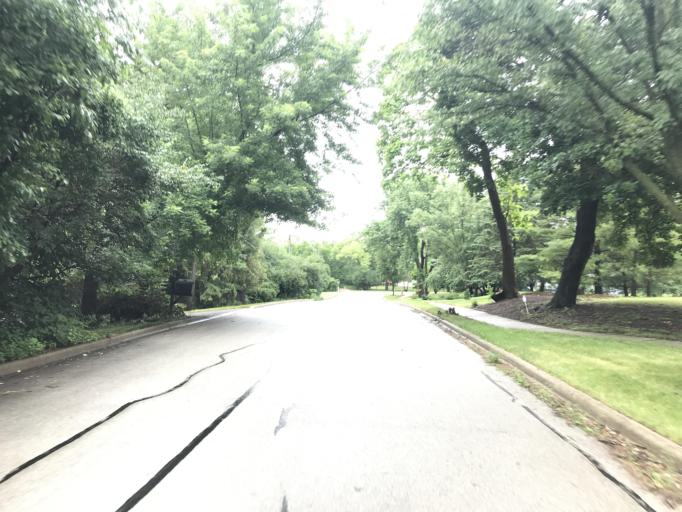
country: US
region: Illinois
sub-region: DuPage County
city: Woodridge
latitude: 41.7432
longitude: -88.0887
